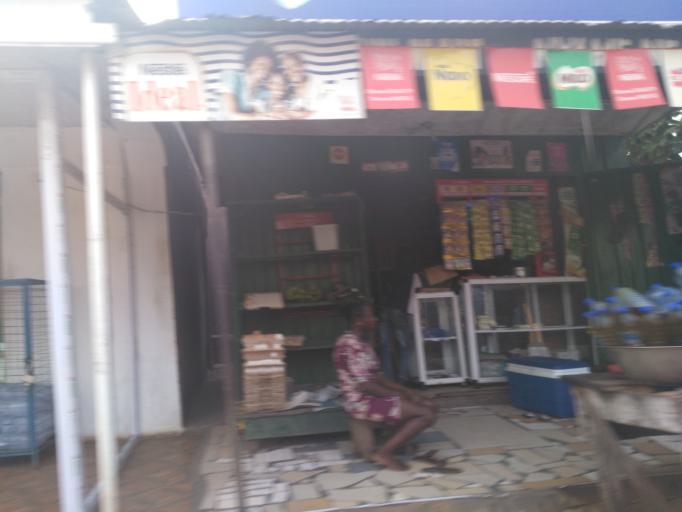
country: GH
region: Ashanti
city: Kumasi
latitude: 6.6821
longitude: -1.5967
